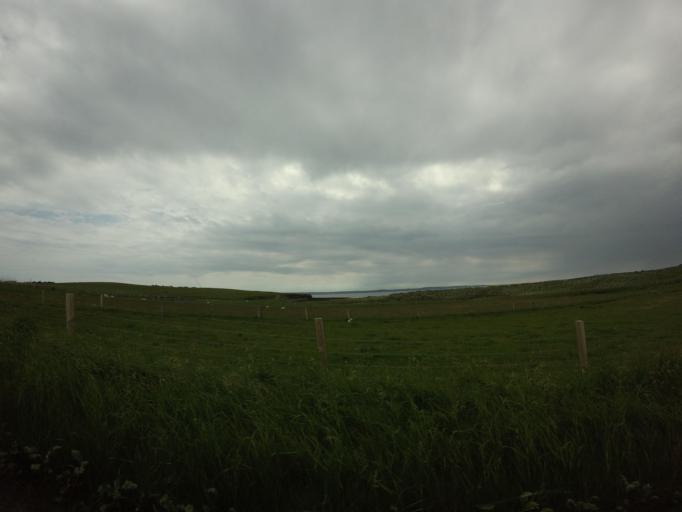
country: GB
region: Scotland
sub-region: Eilean Siar
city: Isle of Lewis
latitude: 58.2708
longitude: -6.3186
